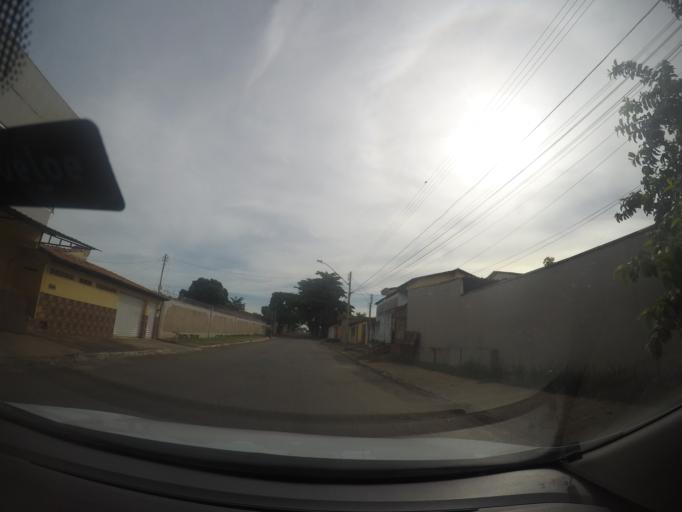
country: BR
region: Goias
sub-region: Goiania
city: Goiania
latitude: -16.6586
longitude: -49.3064
